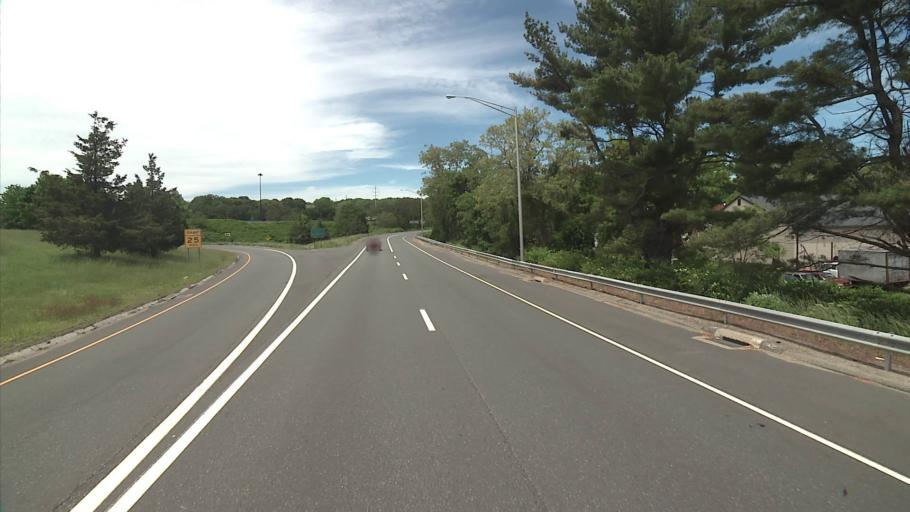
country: US
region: Connecticut
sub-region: New London County
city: New London
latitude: 41.3669
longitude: -72.1039
